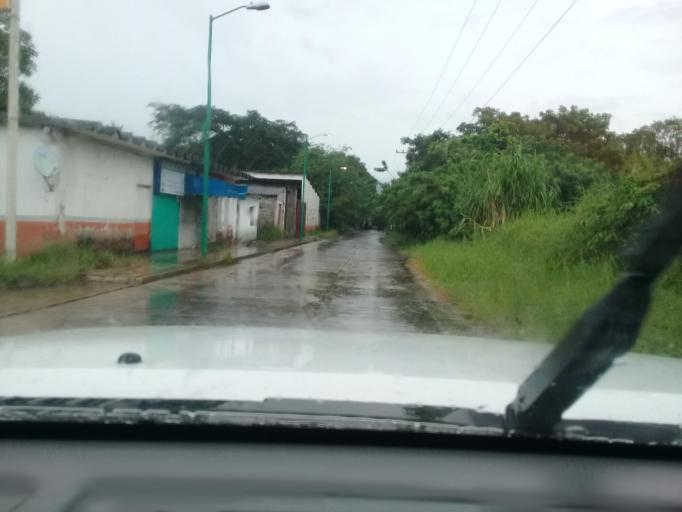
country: MX
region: Veracruz
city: Santiago Tuxtla
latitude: 18.4573
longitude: -95.3090
